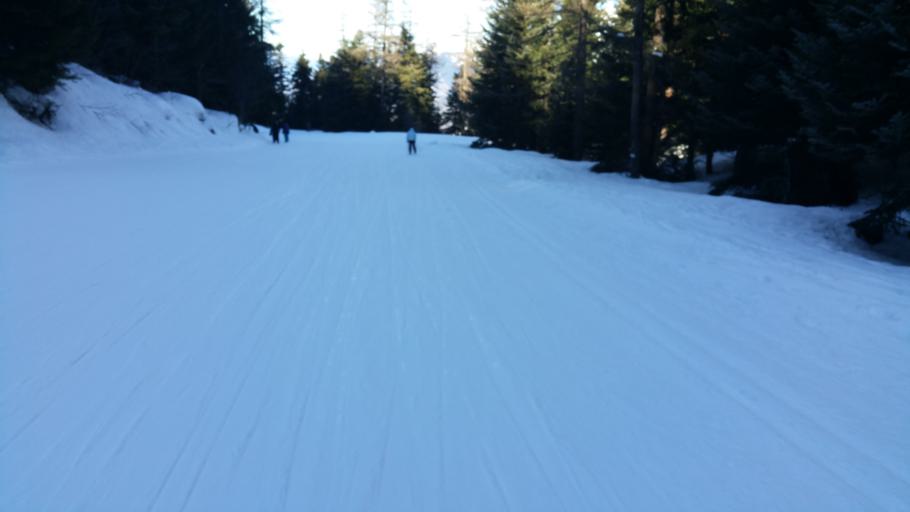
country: FR
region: Rhone-Alpes
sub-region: Departement de la Savoie
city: Valloire
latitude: 45.2217
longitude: 6.4119
